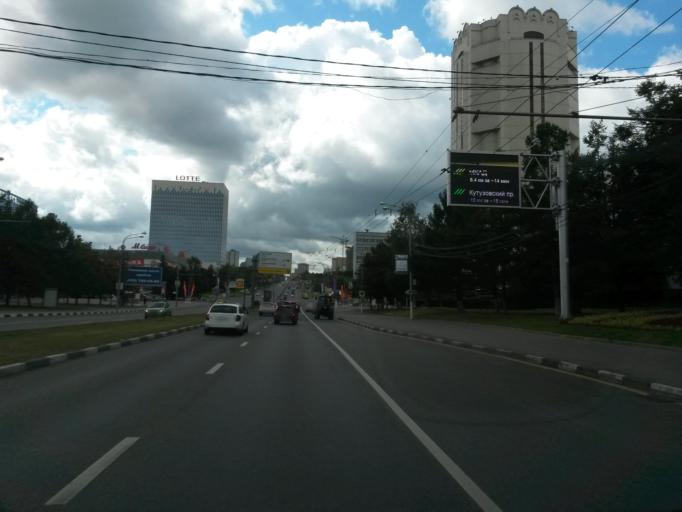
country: RU
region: Moskovskaya
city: Cheremushki
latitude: 55.6575
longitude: 37.5408
